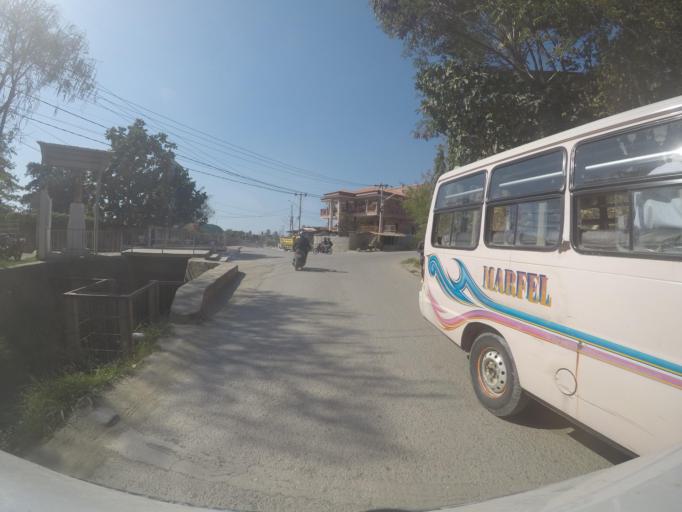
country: TL
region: Dili
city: Dili
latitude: -8.5705
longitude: 125.5429
